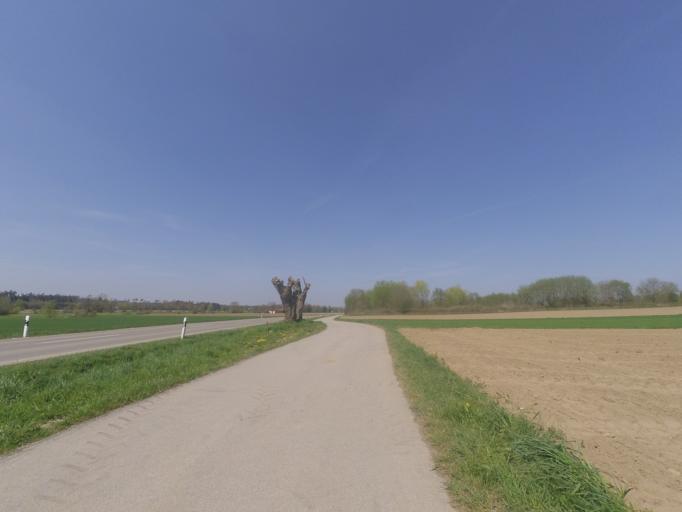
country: DE
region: Bavaria
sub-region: Swabia
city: Weissenhorn
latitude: 48.2818
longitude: 10.1628
